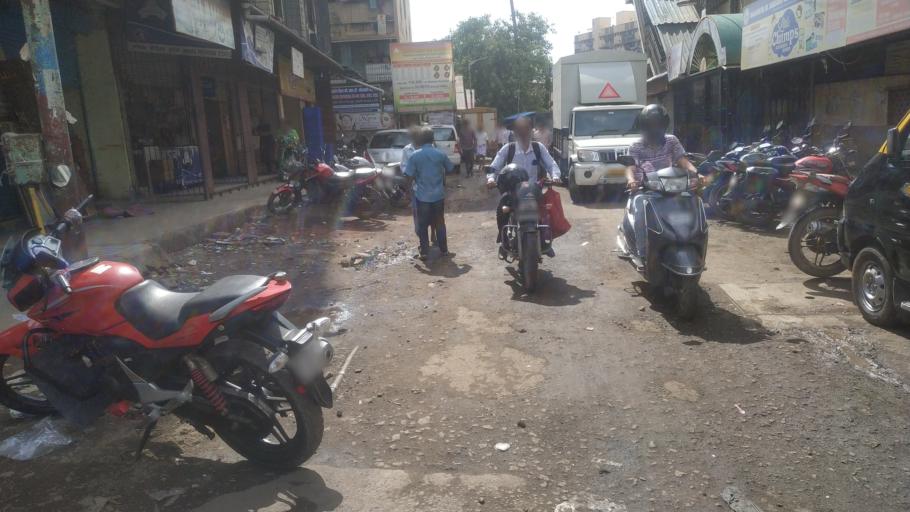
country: IN
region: Maharashtra
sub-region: Mumbai Suburban
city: Mumbai
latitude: 19.0423
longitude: 72.8543
